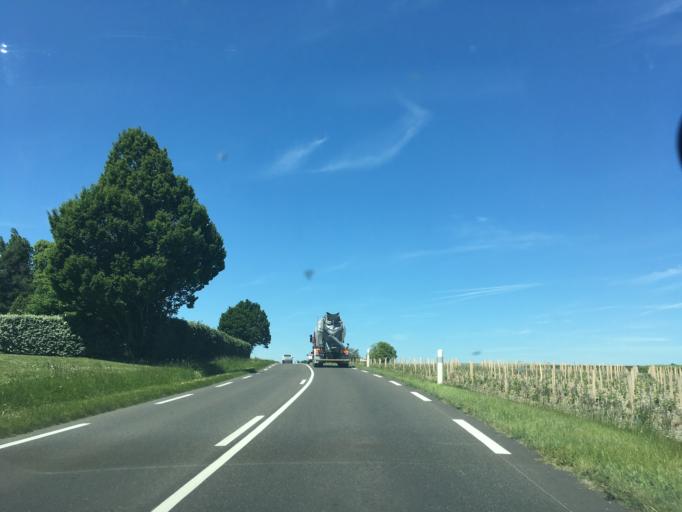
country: FR
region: Aquitaine
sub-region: Departement de la Gironde
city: Listrac-Medoc
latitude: 45.0572
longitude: -0.7957
